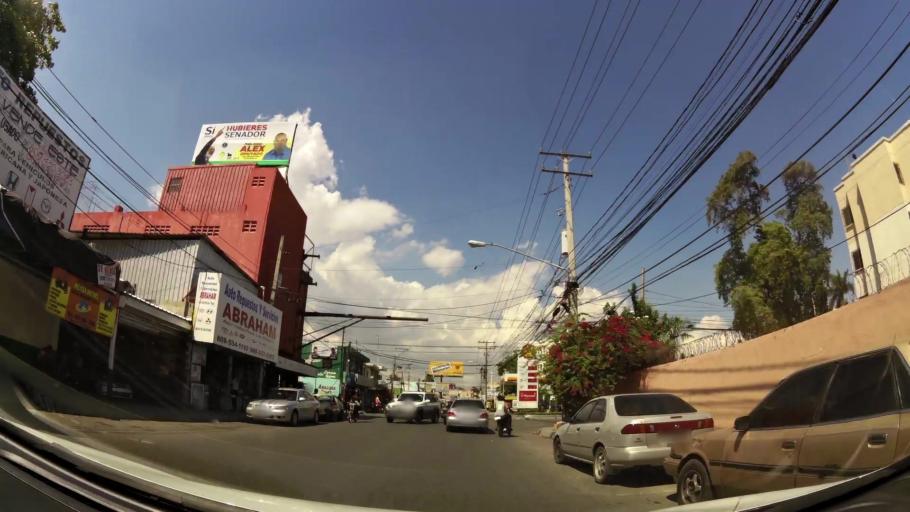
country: DO
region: Nacional
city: Bella Vista
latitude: 18.4598
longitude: -69.9767
